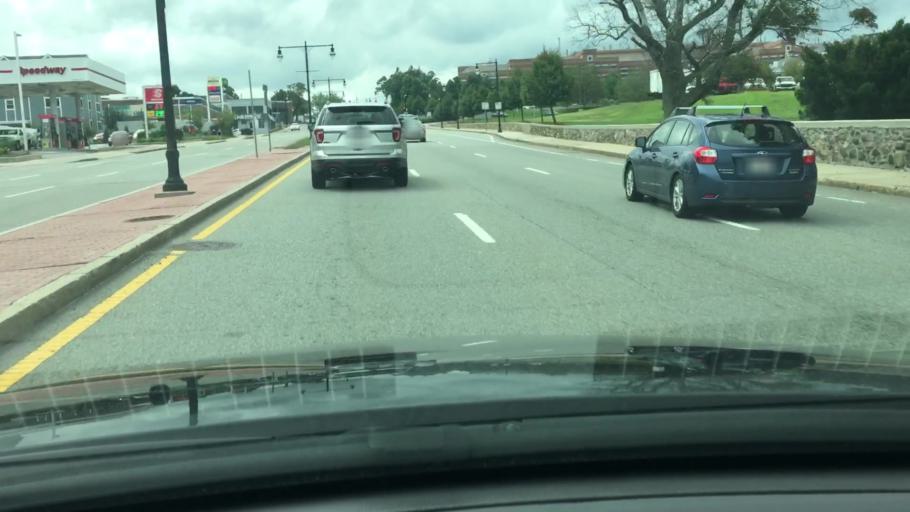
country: US
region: Massachusetts
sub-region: Worcester County
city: Hamilton
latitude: 42.2739
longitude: -71.7646
